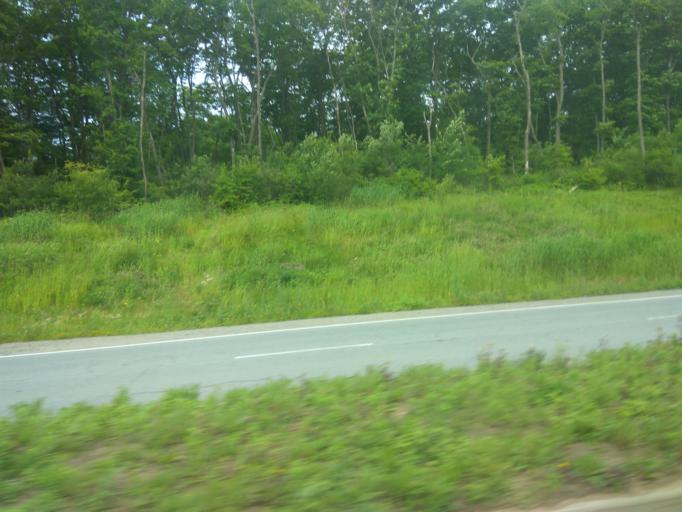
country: RU
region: Primorskiy
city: Russkiy
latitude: 43.0427
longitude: 131.8854
